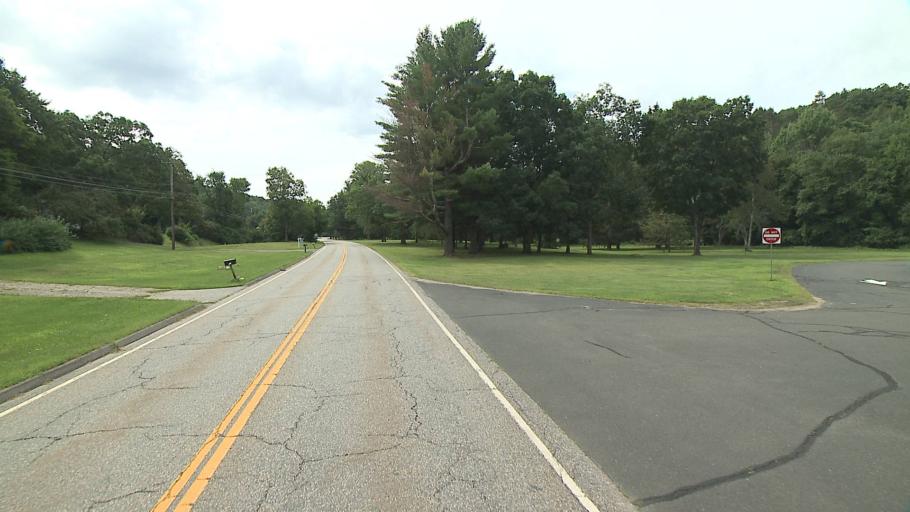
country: US
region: Connecticut
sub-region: Litchfield County
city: New Preston
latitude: 41.6542
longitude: -73.3182
